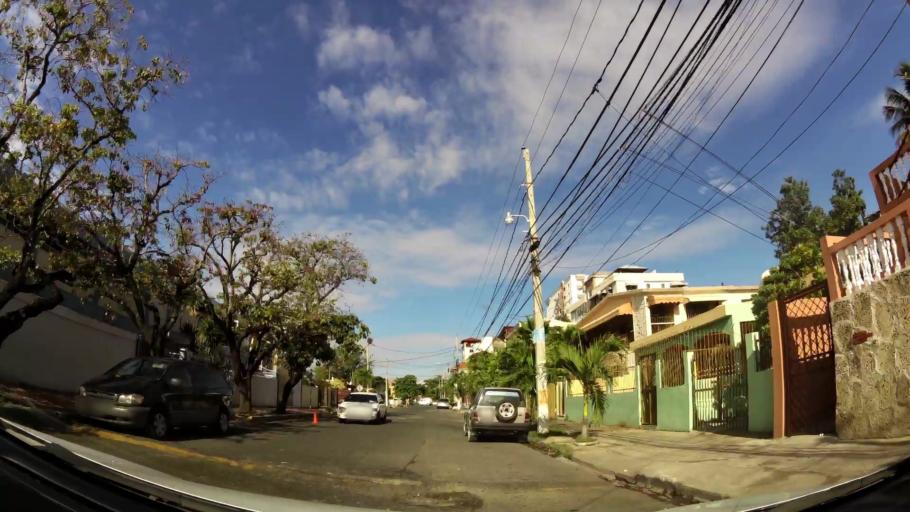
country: DO
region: Santo Domingo
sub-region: Santo Domingo
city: Santo Domingo Este
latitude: 18.4872
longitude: -69.8669
